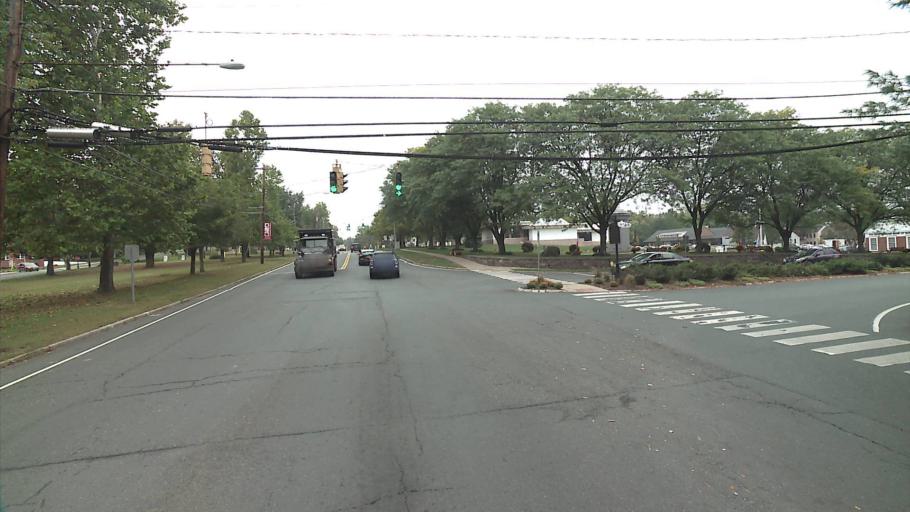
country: US
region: Connecticut
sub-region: Hartford County
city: Suffield Depot
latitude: 41.9812
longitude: -72.6513
